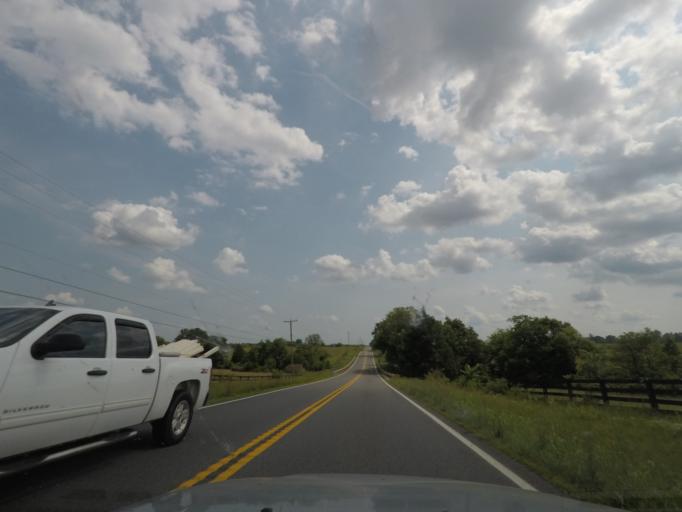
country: US
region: Virginia
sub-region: Orange County
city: Gordonsville
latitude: 38.0473
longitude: -78.1890
